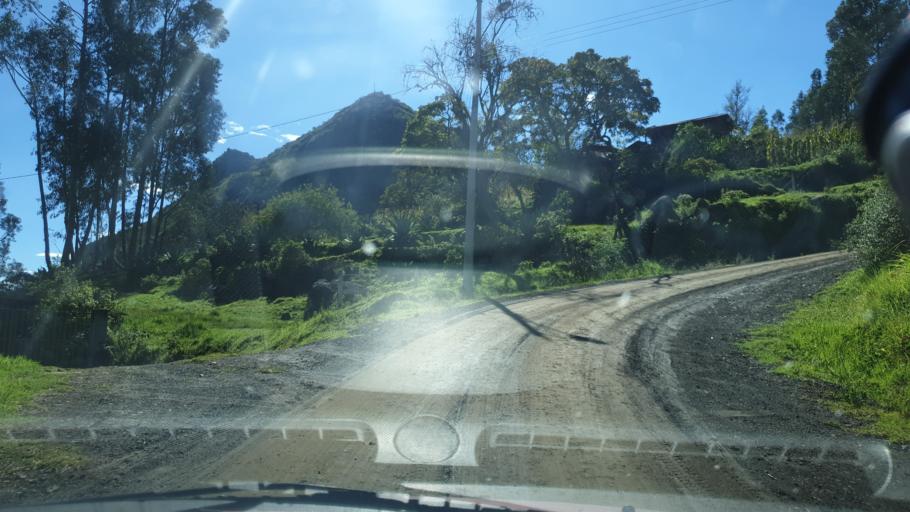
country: EC
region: Azuay
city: Llacao
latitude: -2.8744
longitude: -78.9048
